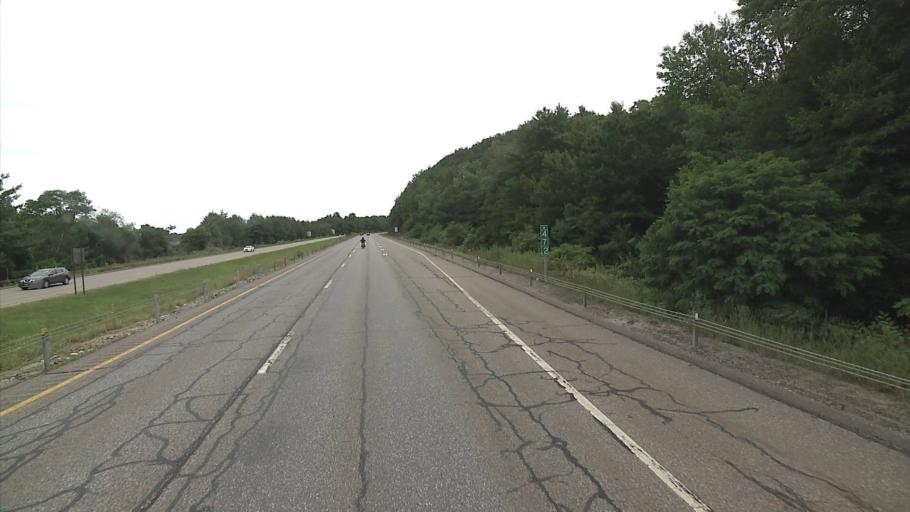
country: US
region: Connecticut
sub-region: Litchfield County
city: Torrington
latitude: 41.7680
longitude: -73.1149
